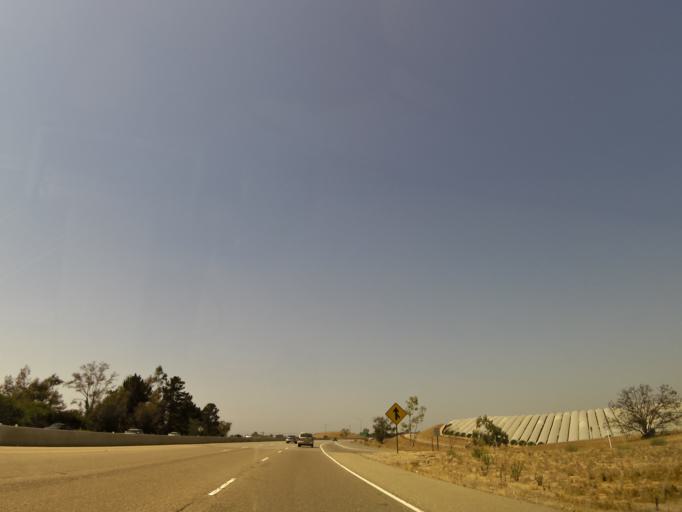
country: US
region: California
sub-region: Santa Barbara County
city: Orcutt
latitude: 34.8886
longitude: -120.4160
